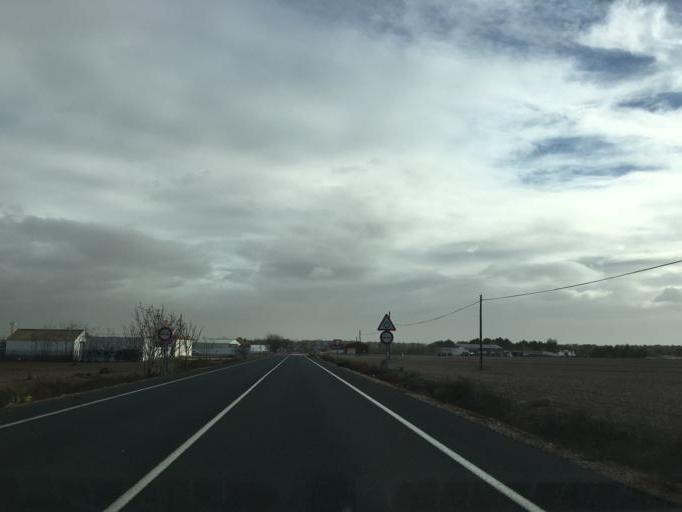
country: ES
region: Castille-La Mancha
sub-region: Provincia de Albacete
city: Albacete
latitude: 38.9995
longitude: -1.8980
